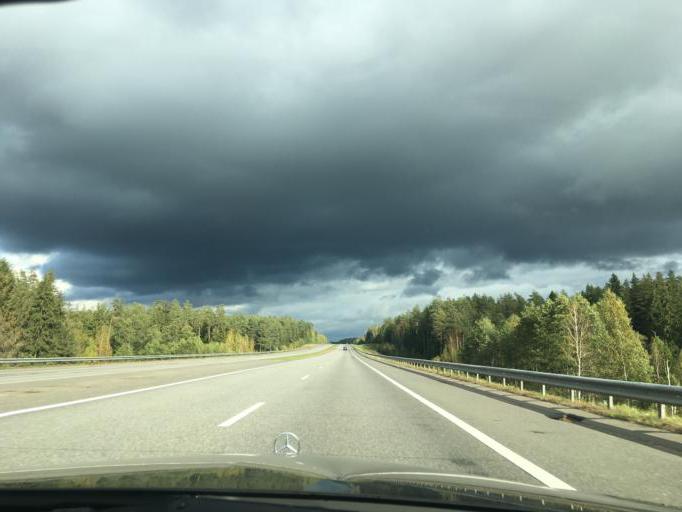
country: BY
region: Minsk
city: Bobr
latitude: 54.4032
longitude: 29.4697
